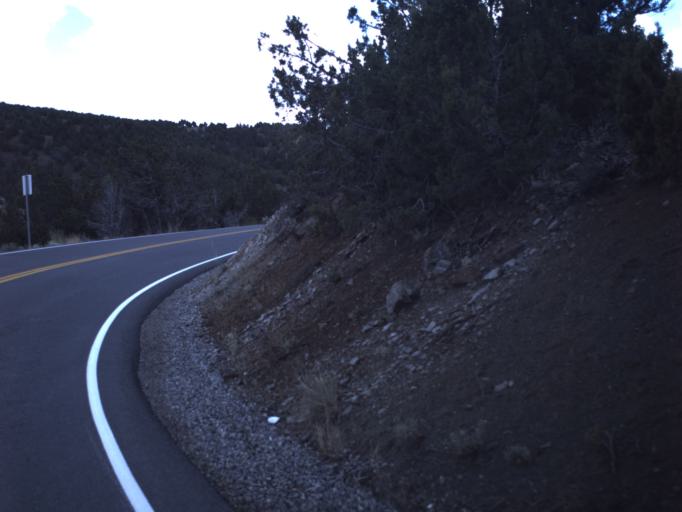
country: US
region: Utah
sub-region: Tooele County
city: Grantsville
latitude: 40.3458
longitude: -112.5646
